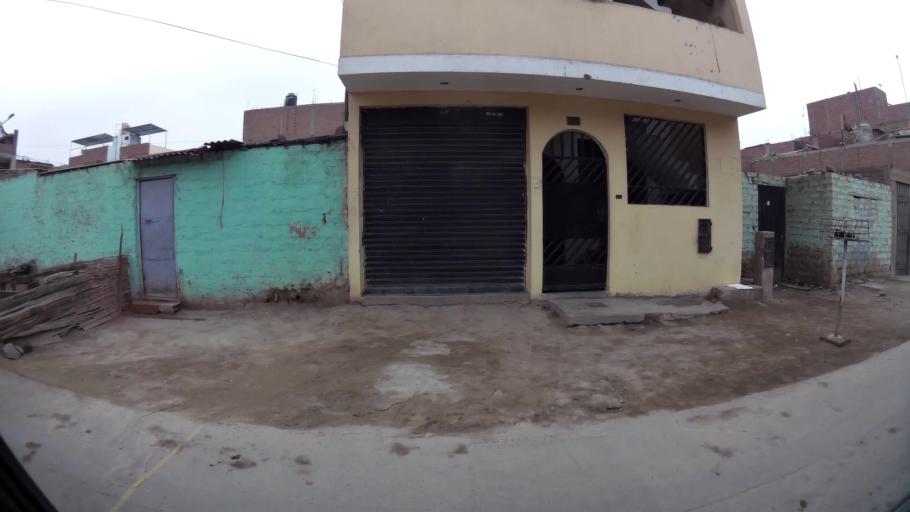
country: PE
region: Lima
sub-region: Lima
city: Independencia
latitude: -11.9611
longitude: -77.0832
